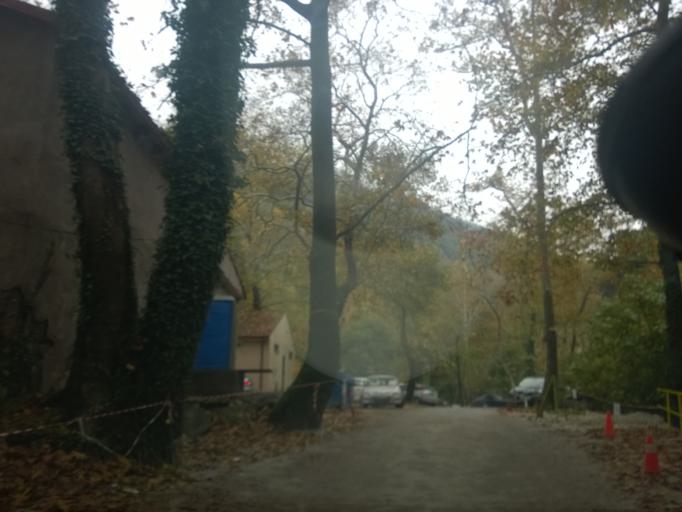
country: GR
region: Central Macedonia
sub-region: Nomos Pellis
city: Loutraki
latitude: 40.9701
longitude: 21.9166
